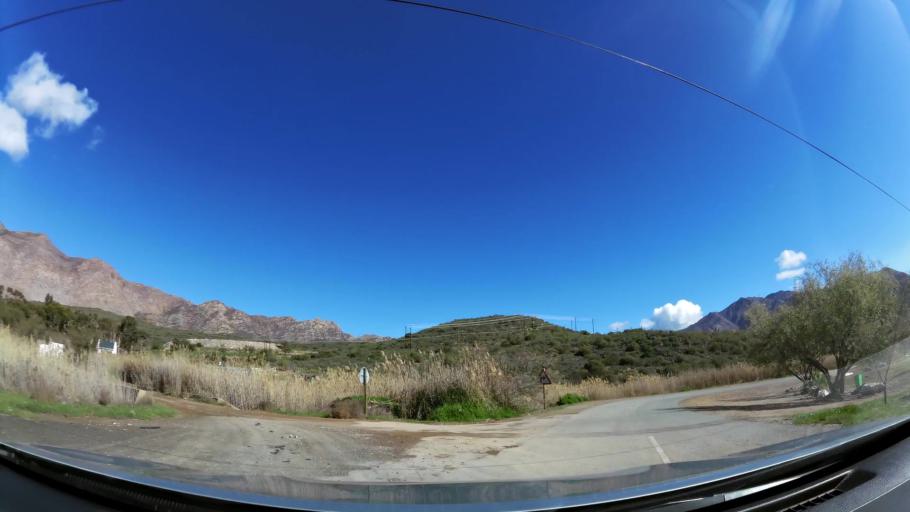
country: ZA
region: Western Cape
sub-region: Cape Winelands District Municipality
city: Ashton
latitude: -33.7919
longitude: 20.1374
